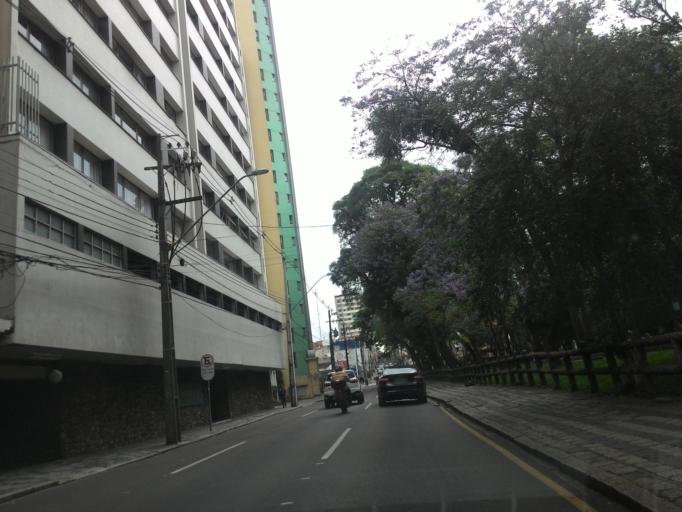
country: BR
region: Parana
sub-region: Curitiba
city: Curitiba
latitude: -25.4267
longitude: -49.2672
